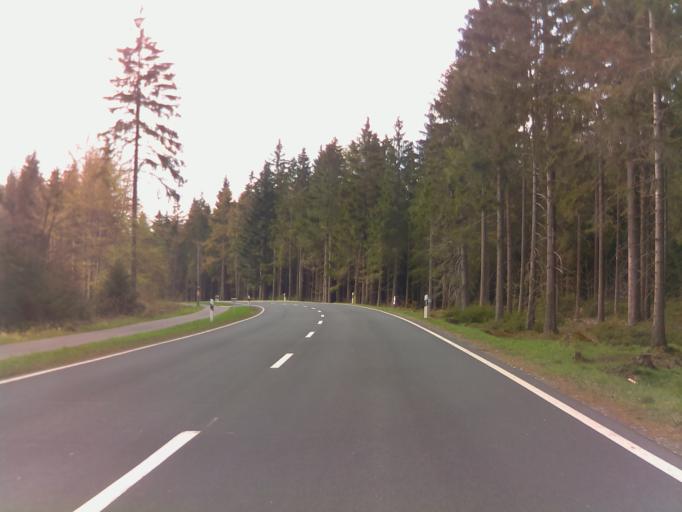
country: DE
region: Bavaria
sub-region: Upper Franconia
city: Ludwigsstadt
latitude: 50.4484
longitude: 11.3588
